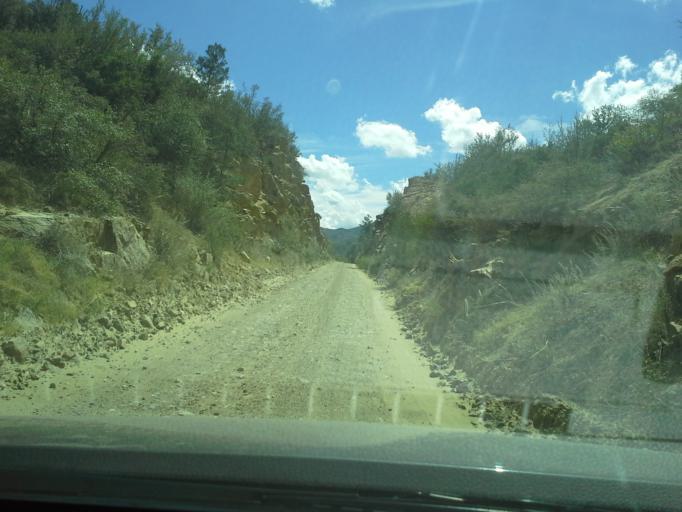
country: US
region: Arizona
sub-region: Yavapai County
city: Mayer
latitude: 34.2461
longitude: -112.2976
